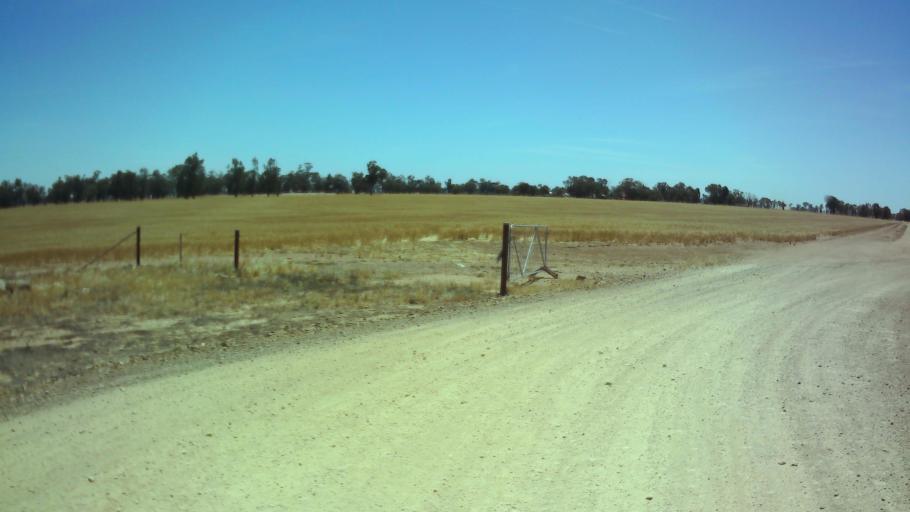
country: AU
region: New South Wales
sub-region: Weddin
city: Grenfell
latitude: -34.0539
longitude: 147.7662
